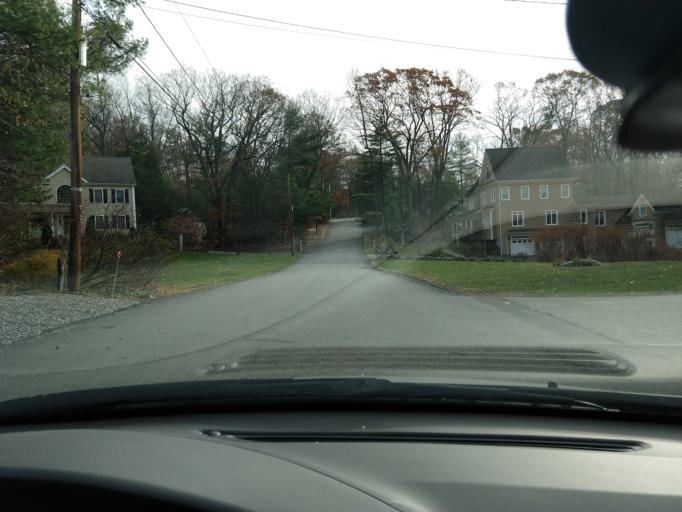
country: US
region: Massachusetts
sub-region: Middlesex County
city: Bedford
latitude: 42.4936
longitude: -71.2493
